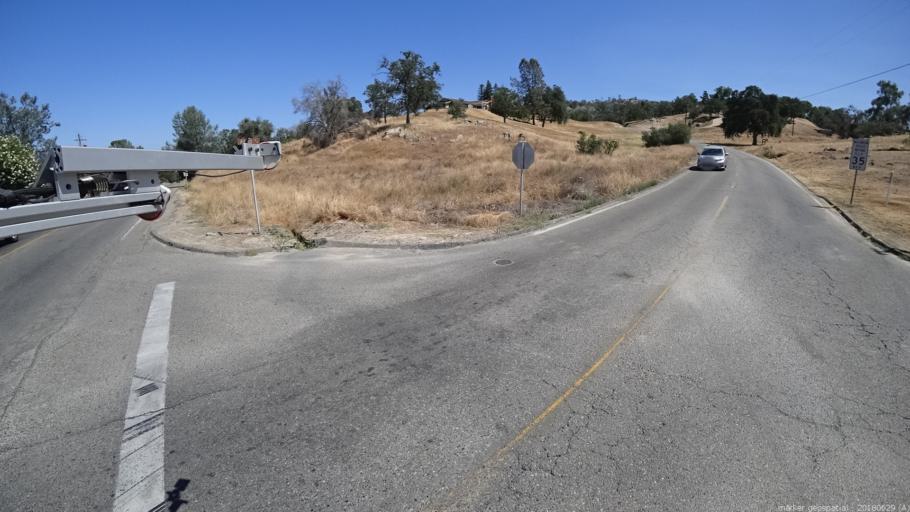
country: US
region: California
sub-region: Madera County
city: Yosemite Lakes
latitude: 37.1696
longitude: -119.7563
